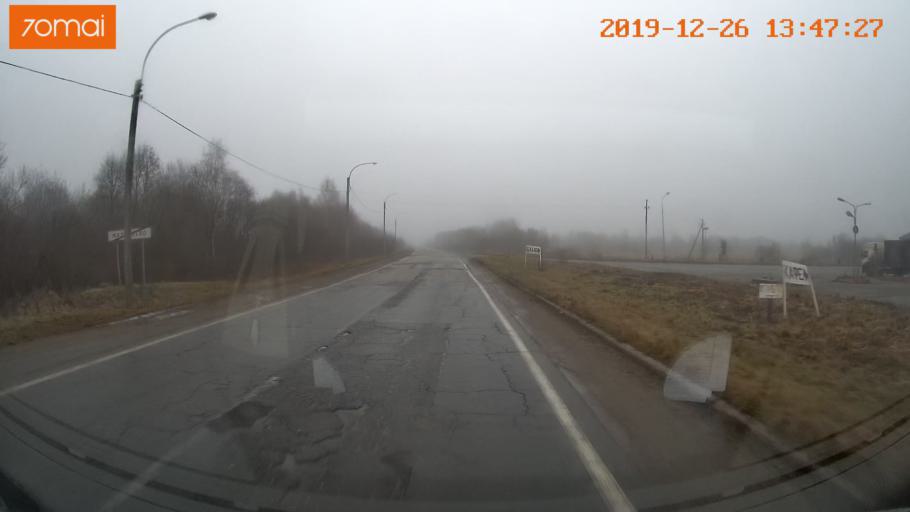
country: RU
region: Vologda
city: Sheksna
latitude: 58.6848
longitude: 38.5342
